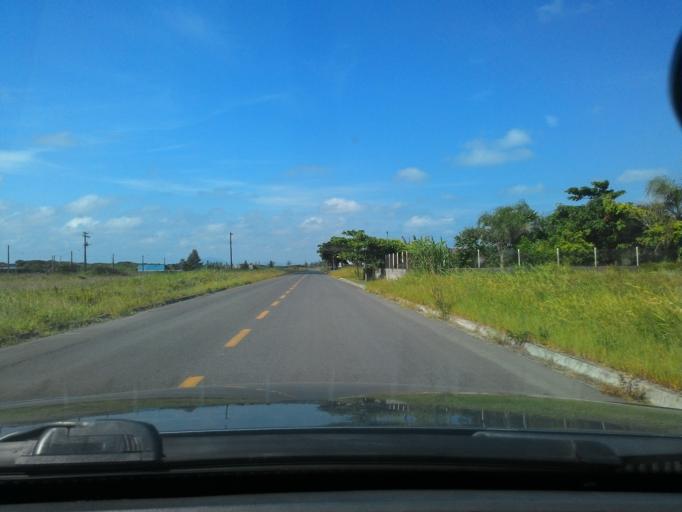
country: BR
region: Sao Paulo
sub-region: Iguape
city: Iguape
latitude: -24.8230
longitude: -47.6608
